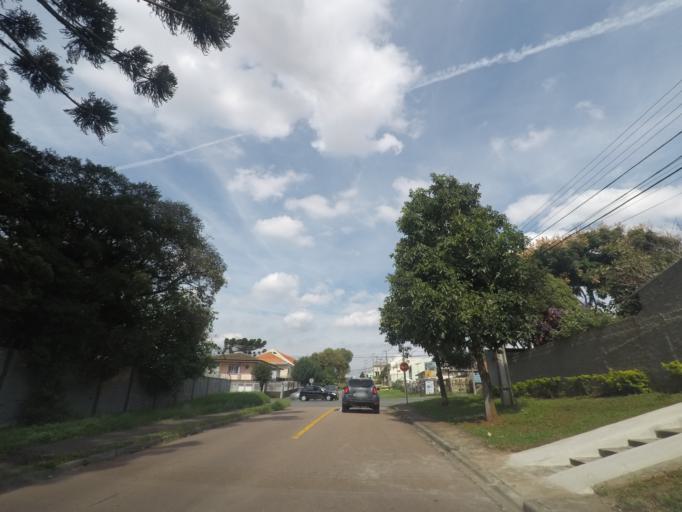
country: BR
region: Parana
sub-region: Sao Jose Dos Pinhais
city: Sao Jose dos Pinhais
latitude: -25.4919
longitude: -49.2590
